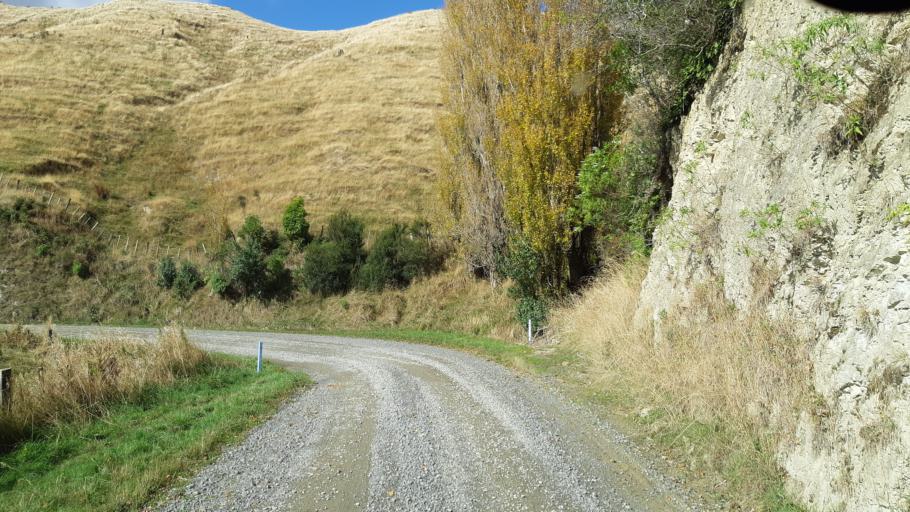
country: NZ
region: Manawatu-Wanganui
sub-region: Ruapehu District
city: Waiouru
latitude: -39.7695
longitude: 175.6745
